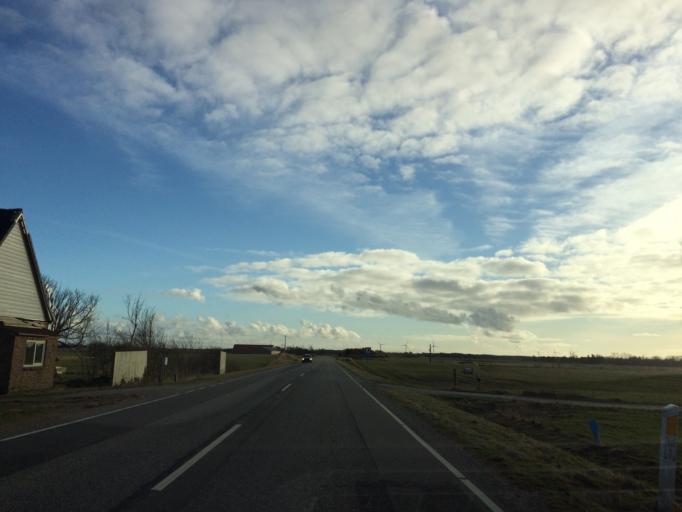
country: DK
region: Central Jutland
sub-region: Lemvig Kommune
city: Lemvig
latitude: 56.4396
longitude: 8.2965
